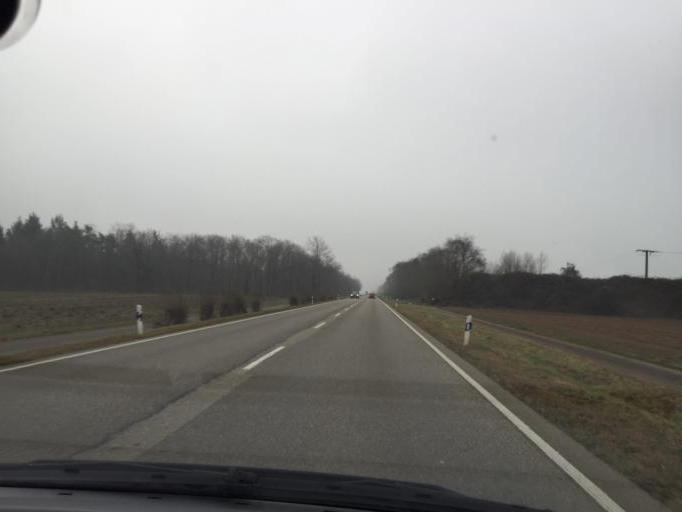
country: DE
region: Baden-Wuerttemberg
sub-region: Freiburg Region
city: Ihringen
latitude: 47.9932
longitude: 7.6332
